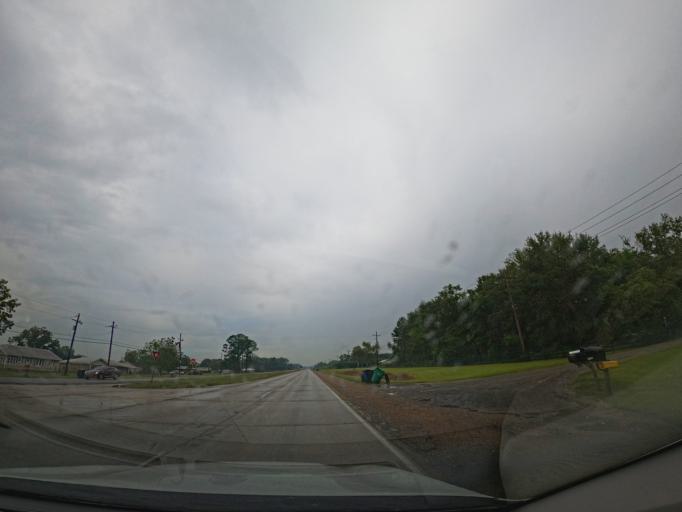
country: US
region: Louisiana
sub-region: Iberia Parish
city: Delcambre
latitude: 29.9653
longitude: -91.9151
